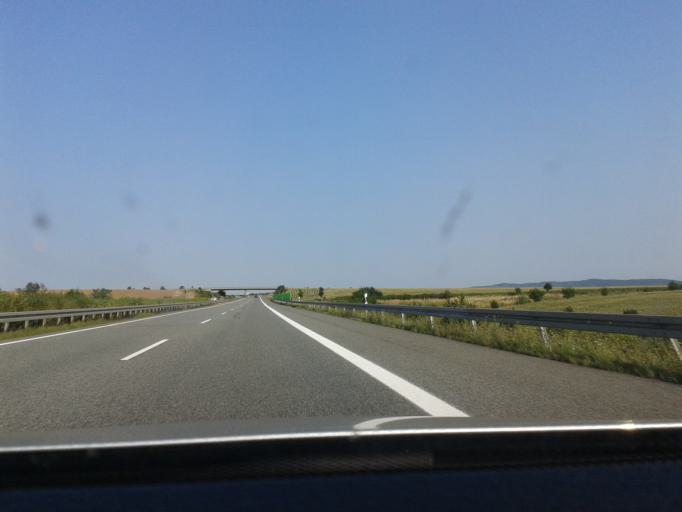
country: DE
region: Thuringia
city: Gorsbach
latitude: 51.4689
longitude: 10.9431
